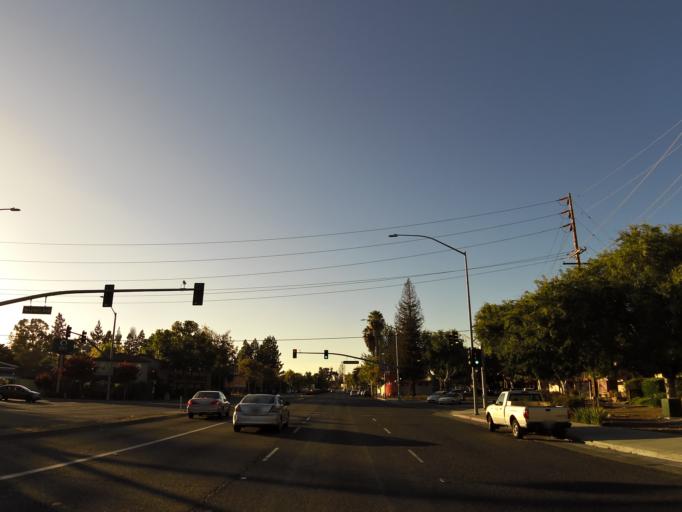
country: US
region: California
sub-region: Santa Clara County
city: Los Altos
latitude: 37.4117
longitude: -122.1243
